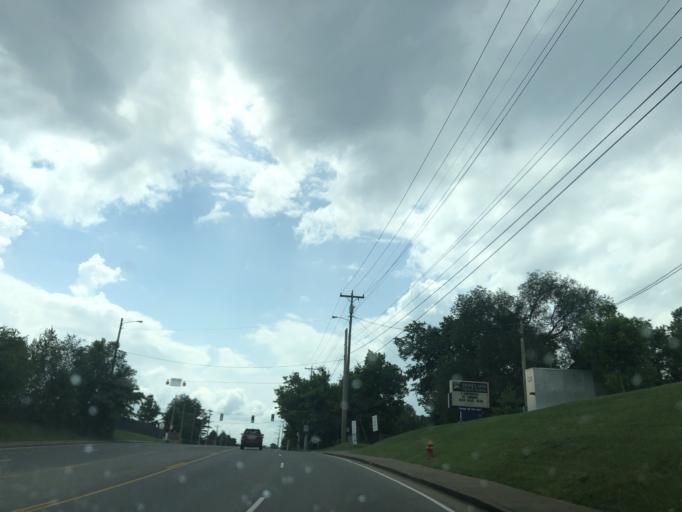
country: US
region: Tennessee
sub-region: Davidson County
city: Lakewood
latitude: 36.1671
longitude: -86.6560
